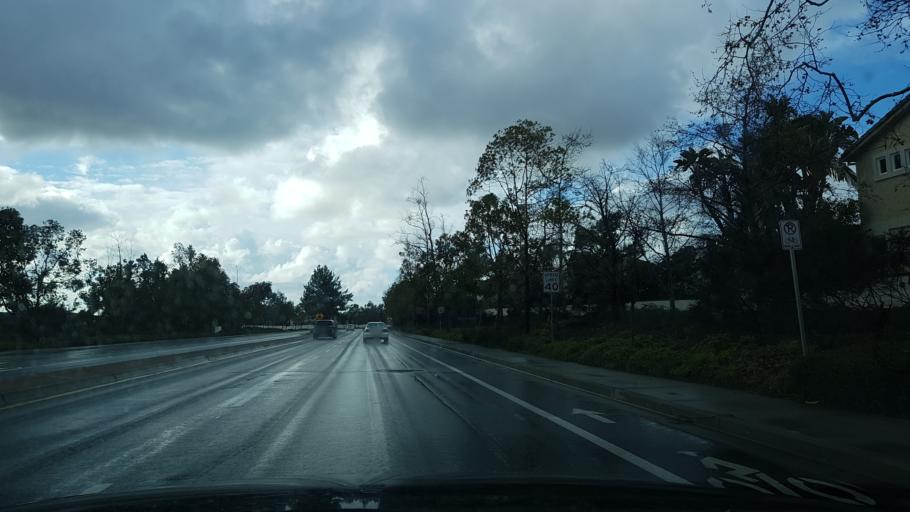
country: US
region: California
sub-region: San Diego County
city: Fairbanks Ranch
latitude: 32.9319
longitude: -117.2003
